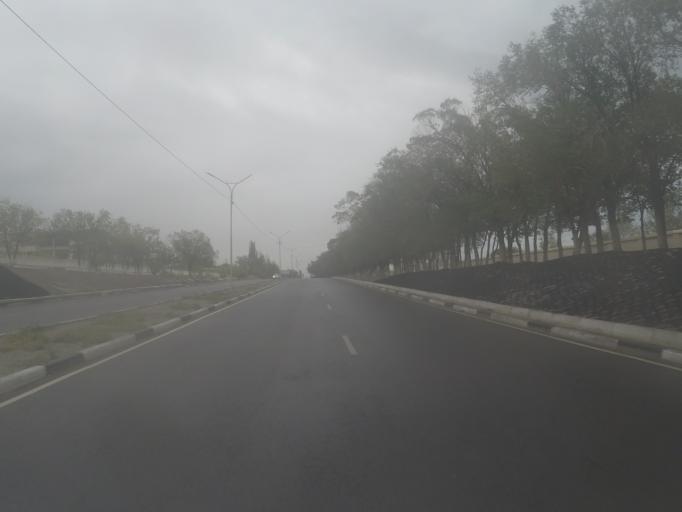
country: KG
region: Ysyk-Koel
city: Balykchy
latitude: 42.4687
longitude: 76.2307
